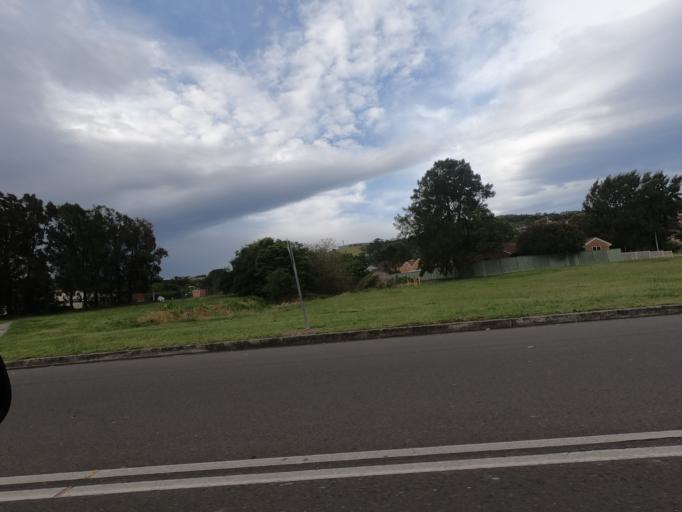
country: AU
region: New South Wales
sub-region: Wollongong
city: Berkeley
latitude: -34.4789
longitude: 150.8546
